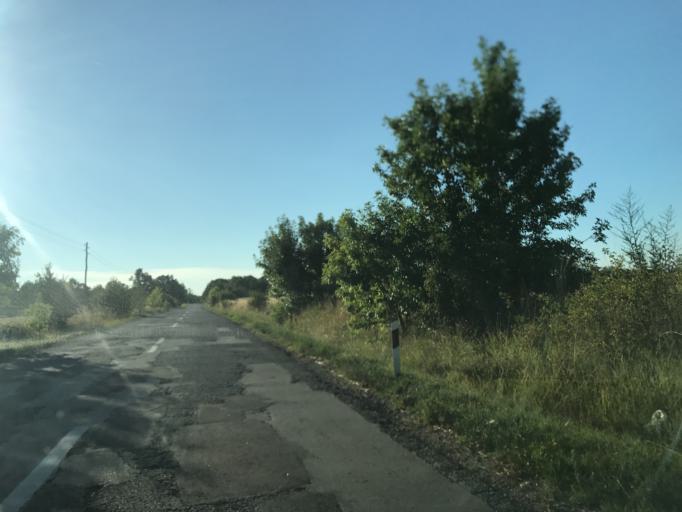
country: RS
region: Central Serbia
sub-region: Borski Okrug
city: Negotin
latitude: 44.2465
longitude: 22.4148
